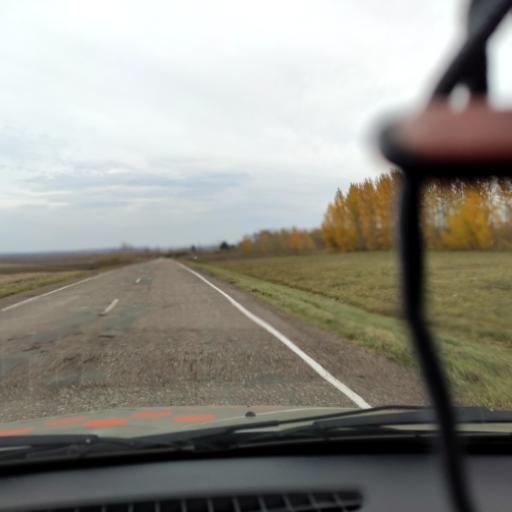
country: RU
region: Bashkortostan
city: Kabakovo
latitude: 54.5245
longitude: 56.0547
